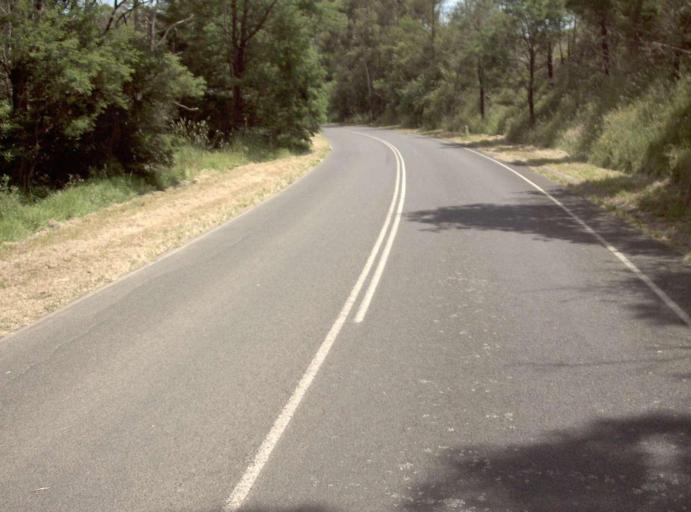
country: AU
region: Victoria
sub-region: Baw Baw
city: Warragul
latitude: -38.5062
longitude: 146.0052
